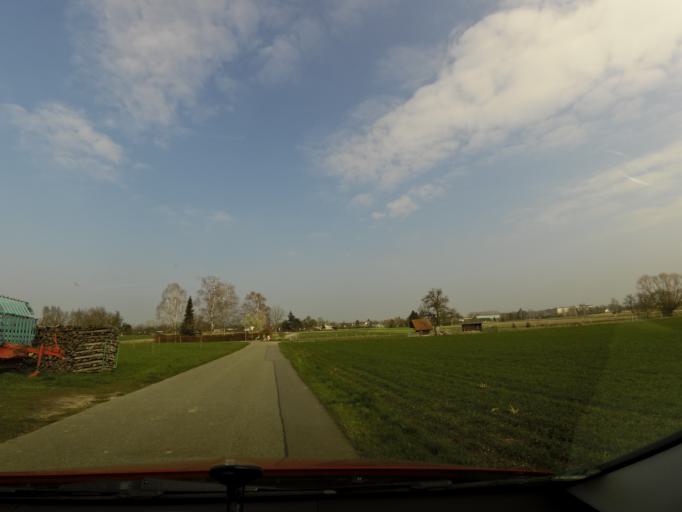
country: DE
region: Baden-Wuerttemberg
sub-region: Freiburg Region
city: Kehl
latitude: 48.5911
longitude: 7.8681
